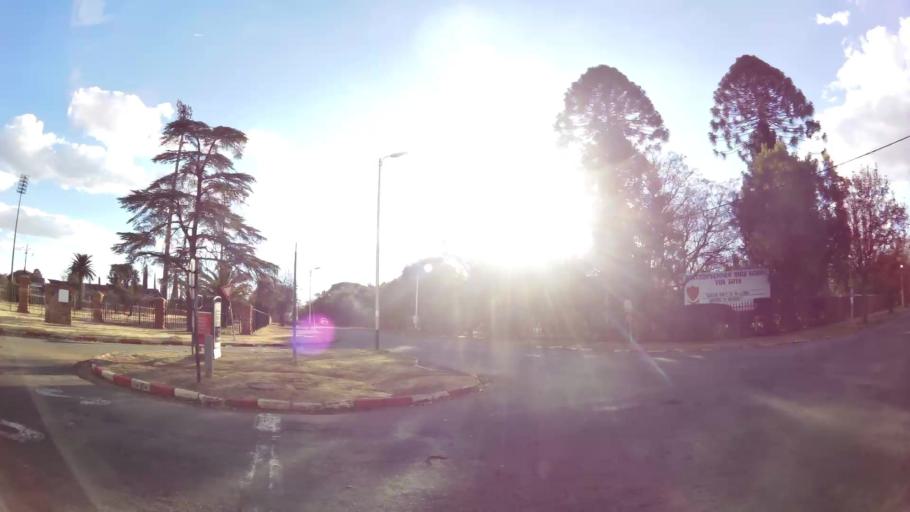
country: ZA
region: North-West
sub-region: Dr Kenneth Kaunda District Municipality
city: Potchefstroom
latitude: -26.7105
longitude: 27.0912
